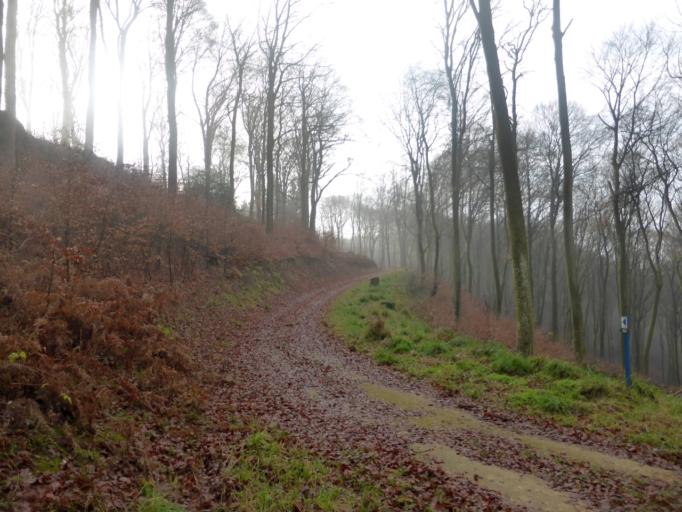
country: LU
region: Luxembourg
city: Rollingen
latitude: 49.7649
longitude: 6.1371
